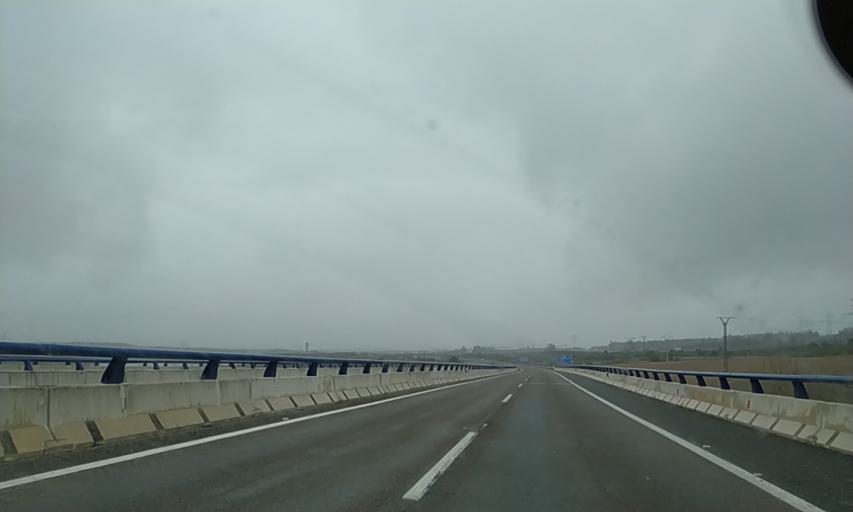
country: ES
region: Extremadura
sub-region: Provincia de Caceres
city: Canaveral
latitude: 39.8087
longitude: -6.3645
